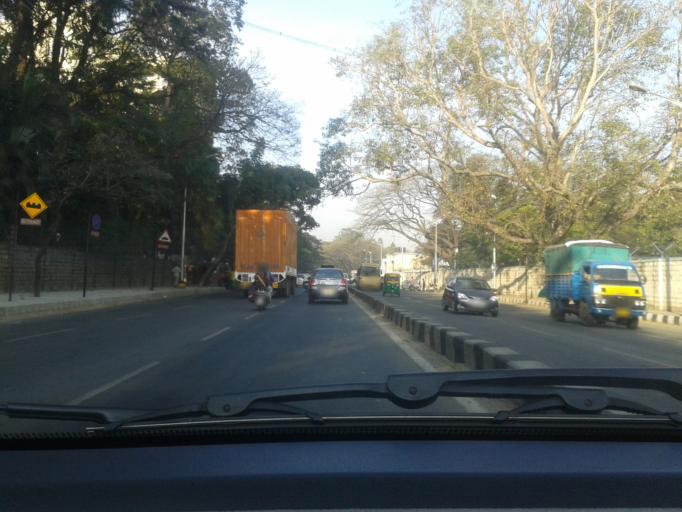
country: IN
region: Karnataka
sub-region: Bangalore Urban
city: Bangalore
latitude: 13.0147
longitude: 77.5803
